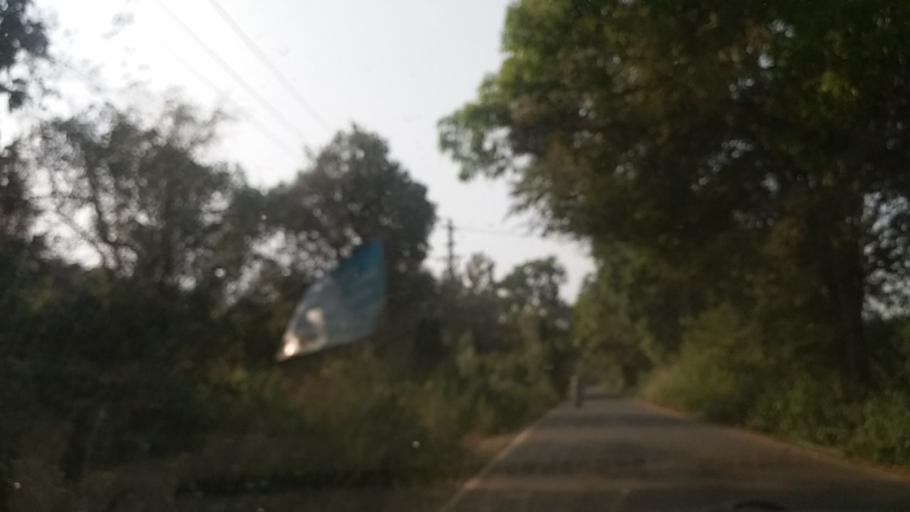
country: IN
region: Goa
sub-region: North Goa
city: Pernem
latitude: 15.7136
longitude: 73.8078
